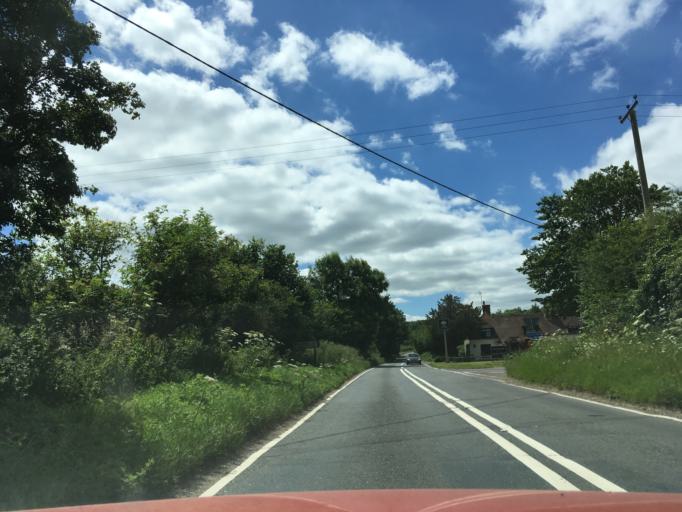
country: GB
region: England
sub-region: Hampshire
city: Highclere
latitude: 51.3284
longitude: -1.3798
